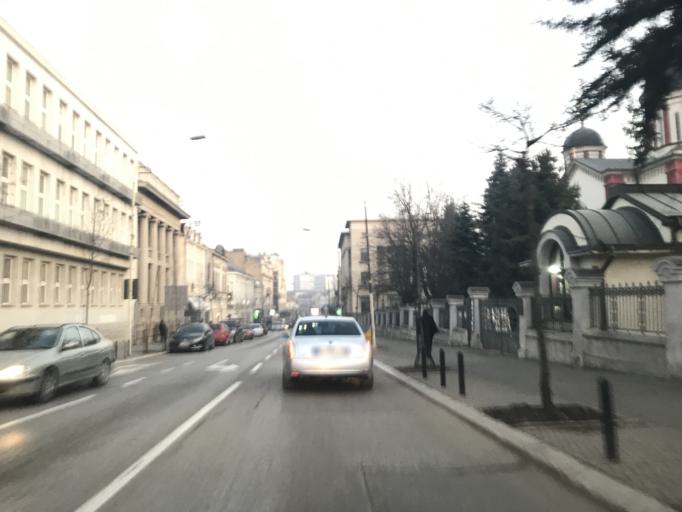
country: RS
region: Central Serbia
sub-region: Sumadijski Okrug
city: Kragujevac
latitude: 44.0125
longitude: 20.9120
